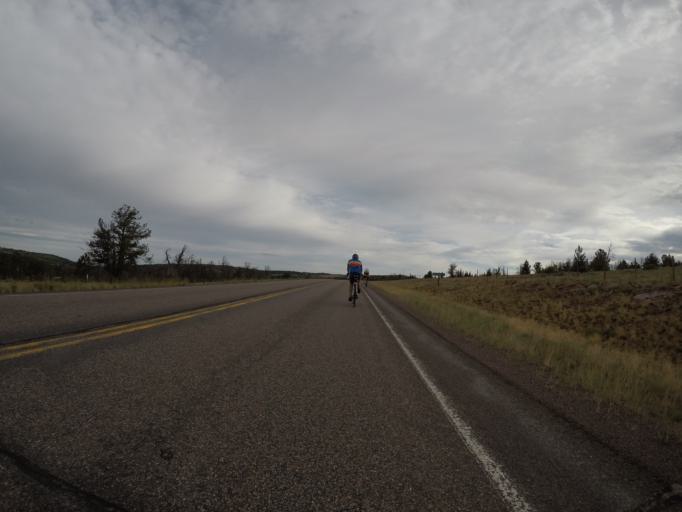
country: US
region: Wyoming
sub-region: Albany County
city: Laramie
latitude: 41.2440
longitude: -105.4363
